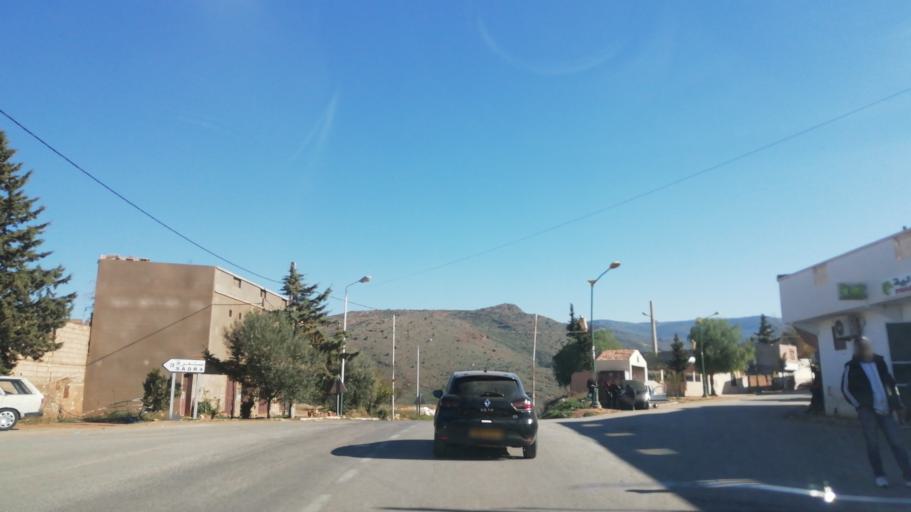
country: DZ
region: Tlemcen
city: Beni Mester
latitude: 34.8424
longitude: -1.4726
